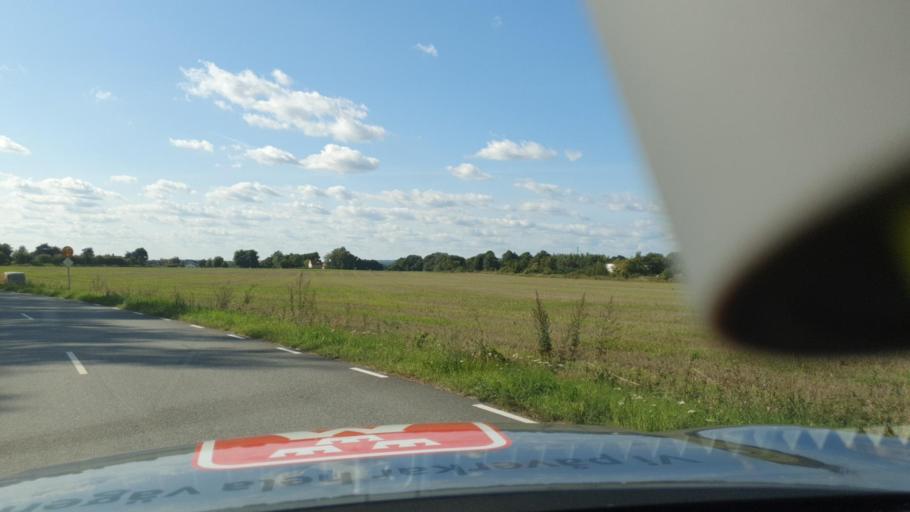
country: SE
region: Skane
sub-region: Bromolla Kommun
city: Bromoella
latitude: 56.0857
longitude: 14.4901
